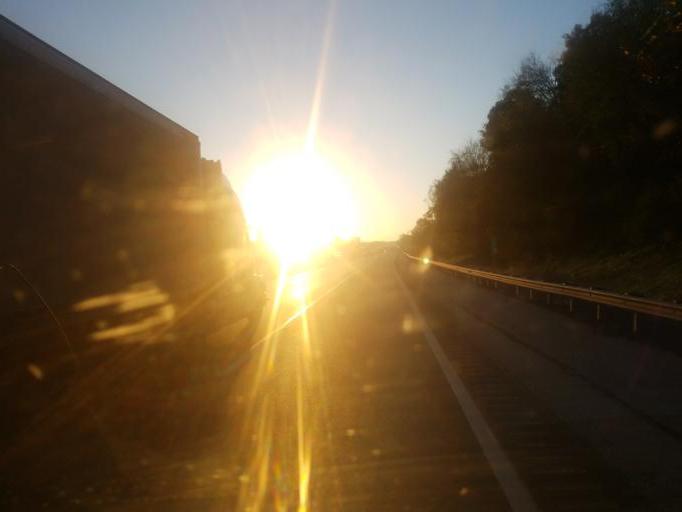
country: US
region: Pennsylvania
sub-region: Lawrence County
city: Bessemer
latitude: 40.9024
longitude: -80.4882
